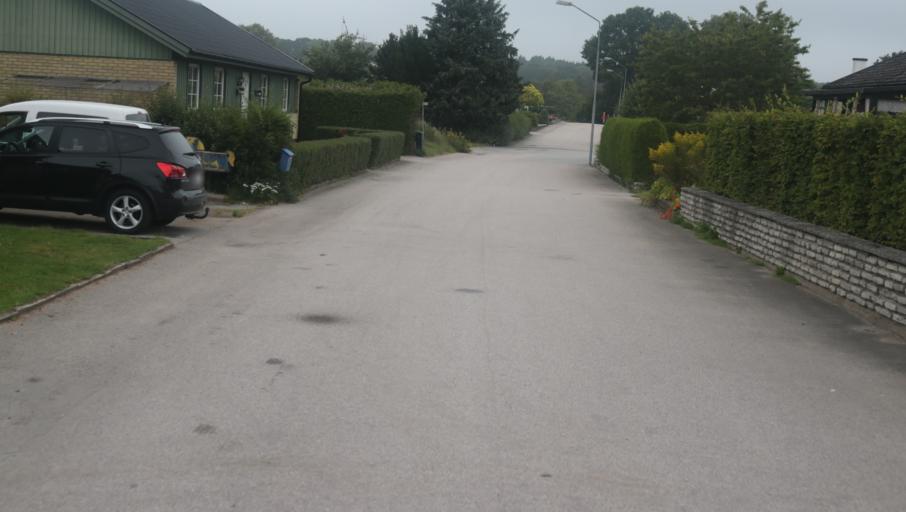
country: SE
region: Blekinge
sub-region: Karlshamns Kommun
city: Karlshamn
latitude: 56.2016
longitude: 14.9442
